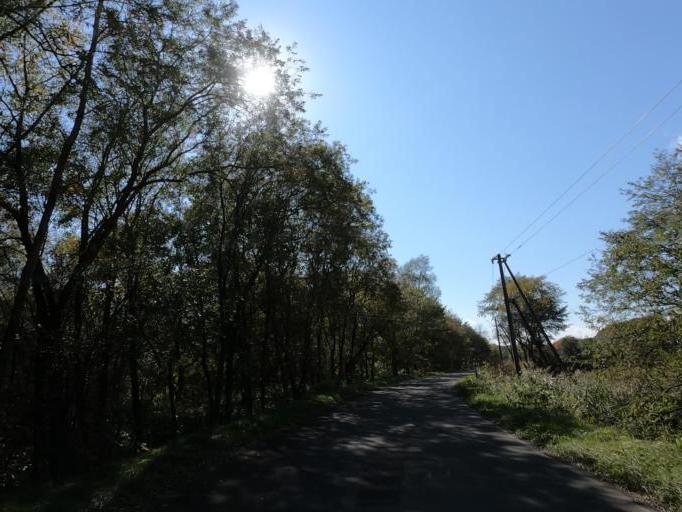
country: JP
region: Hokkaido
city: Otofuke
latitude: 43.2366
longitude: 143.2683
